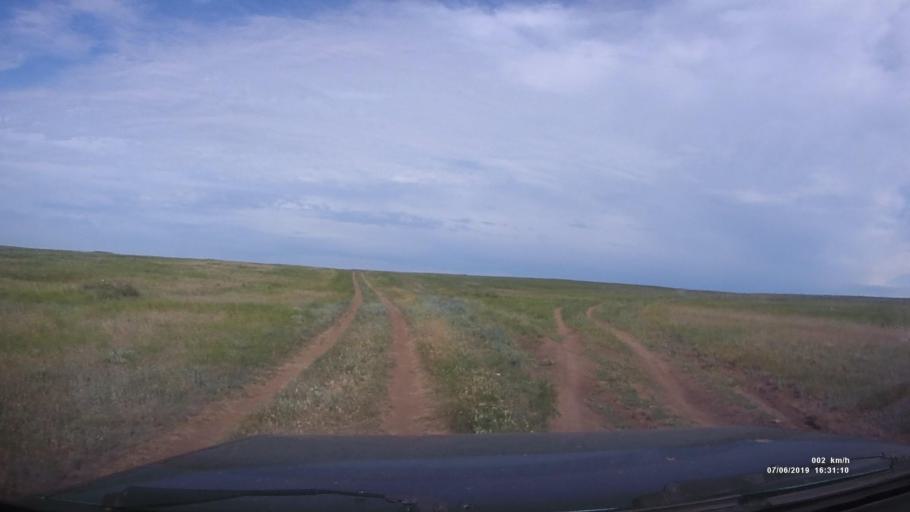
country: RU
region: Rostov
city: Staraya Stanitsa
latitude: 48.2556
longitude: 40.3271
